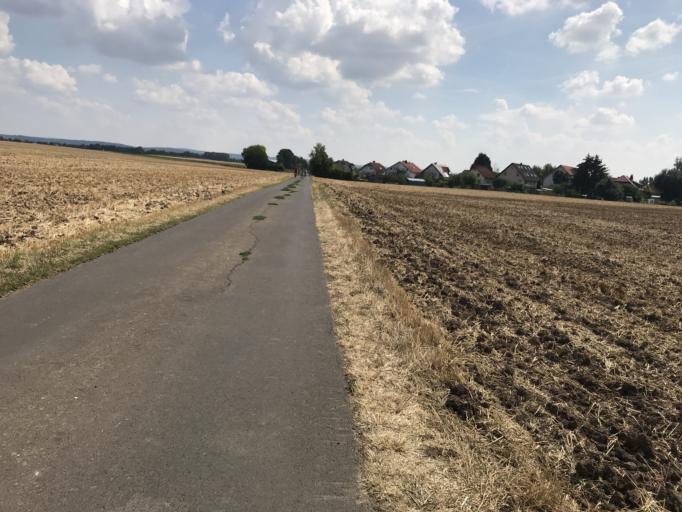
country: DE
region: Hesse
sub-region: Regierungsbezirk Darmstadt
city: Wolfersheim
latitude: 50.4433
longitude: 8.8378
